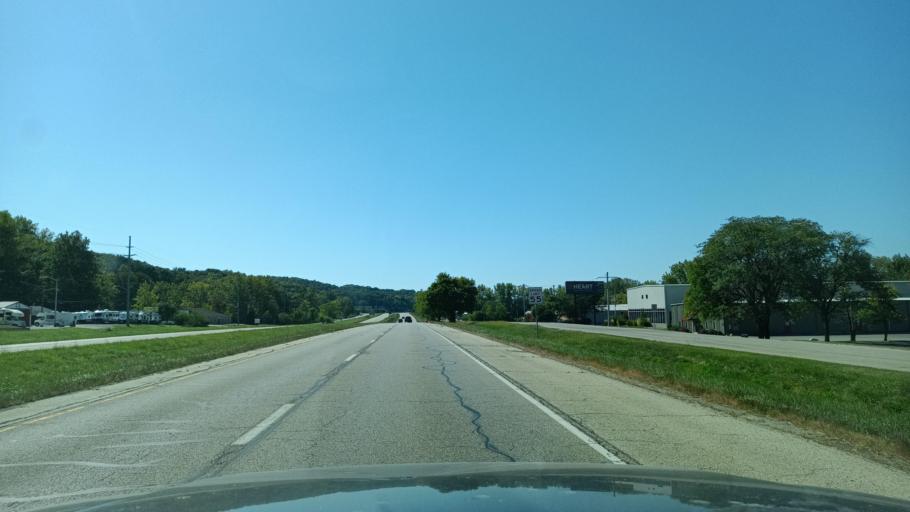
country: US
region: Illinois
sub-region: Peoria County
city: North Peoria
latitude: 40.7026
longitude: -89.5370
